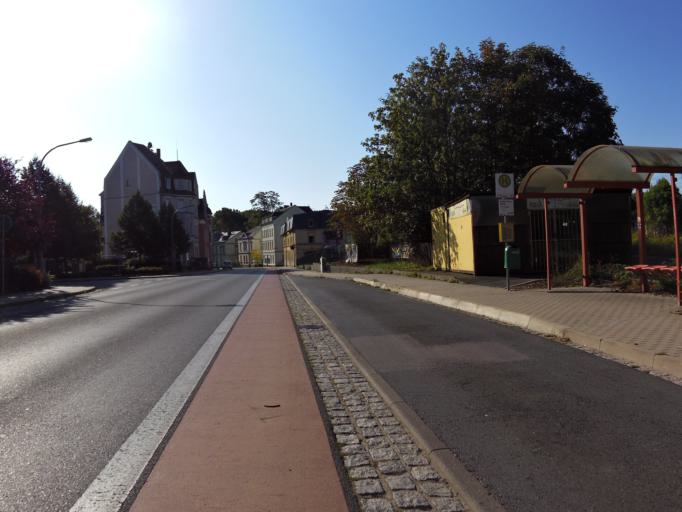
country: DE
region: Saxony
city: Dobeln
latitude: 51.1235
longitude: 13.1027
